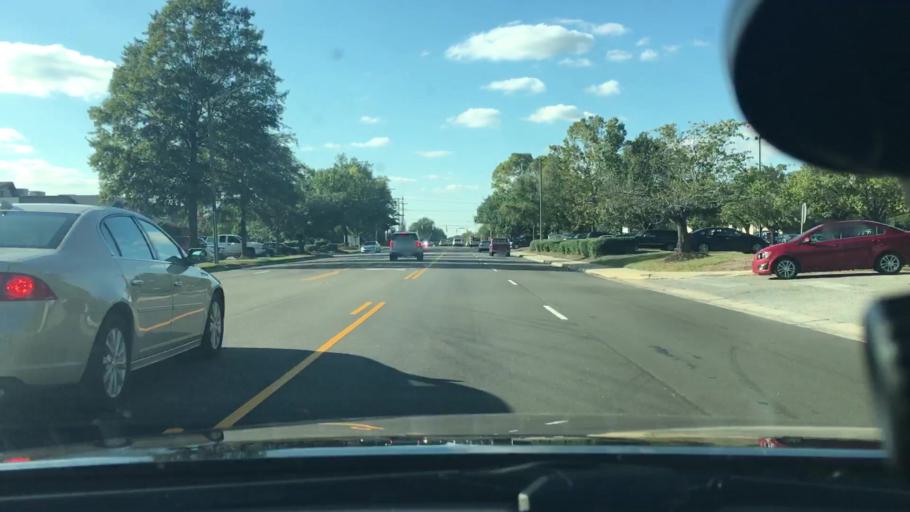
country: US
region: North Carolina
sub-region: Pitt County
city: Greenville
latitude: 35.5842
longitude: -77.3684
